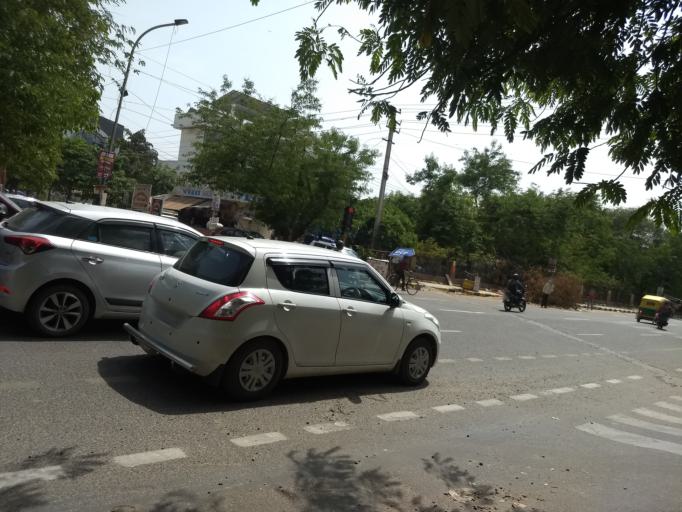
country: IN
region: Haryana
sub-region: Gurgaon
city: Gurgaon
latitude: 28.4681
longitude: 77.0799
